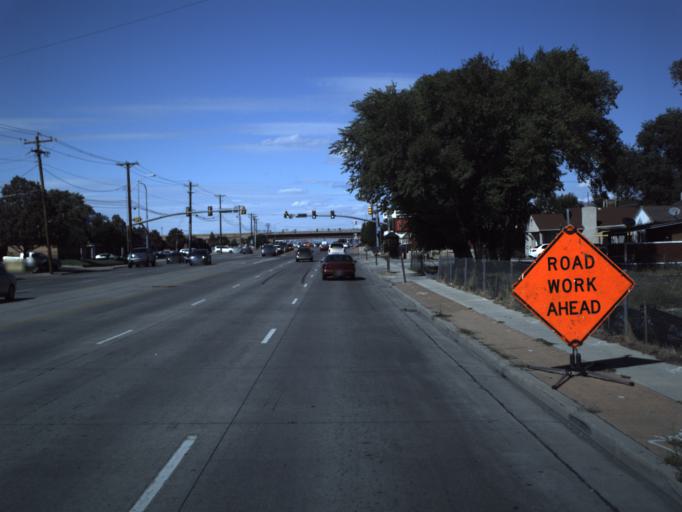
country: US
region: Utah
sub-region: Salt Lake County
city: Centerfield
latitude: 40.7196
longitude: -111.9389
